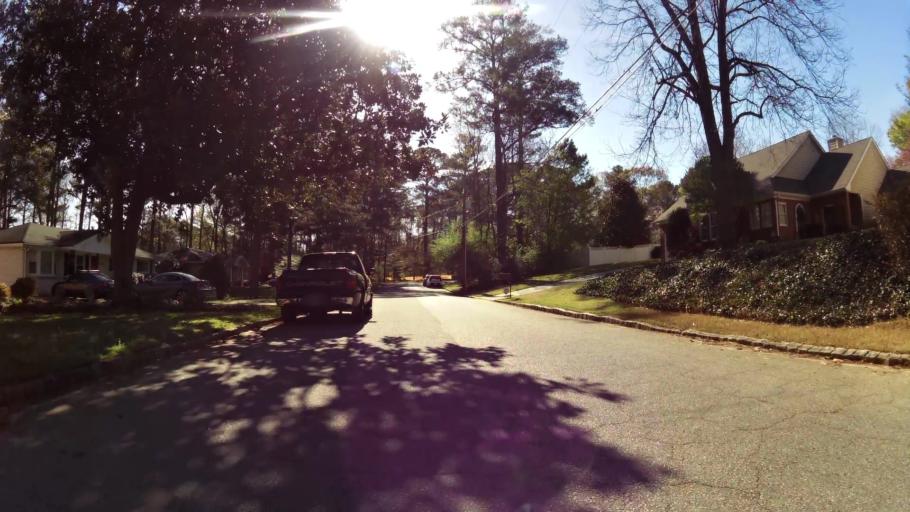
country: US
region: Georgia
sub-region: DeKalb County
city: Clarkston
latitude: 33.8315
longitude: -84.2602
